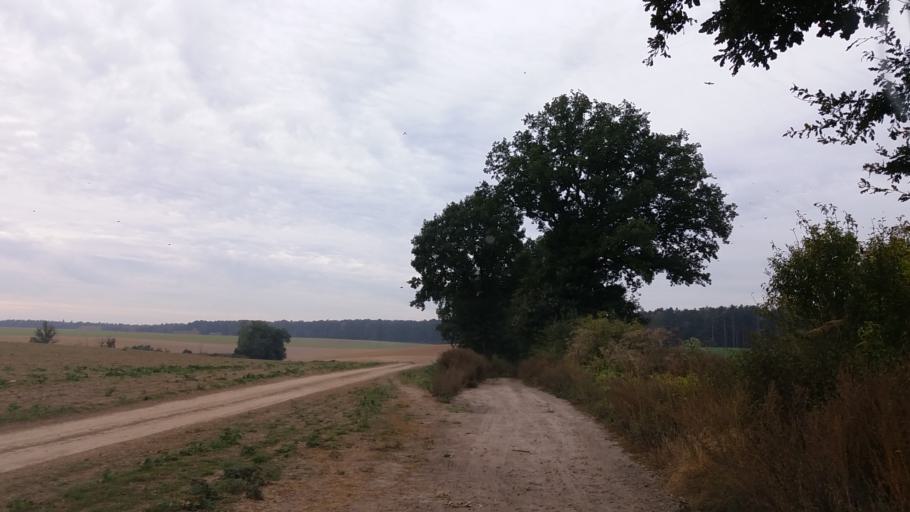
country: PL
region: West Pomeranian Voivodeship
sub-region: Powiat choszczenski
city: Pelczyce
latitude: 53.0835
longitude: 15.2961
